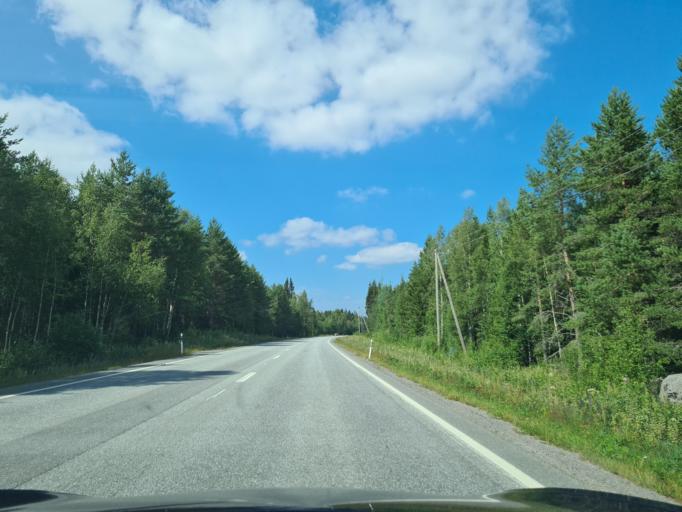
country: FI
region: Ostrobothnia
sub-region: Vaasa
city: Vaasa
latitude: 63.1711
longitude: 21.5827
